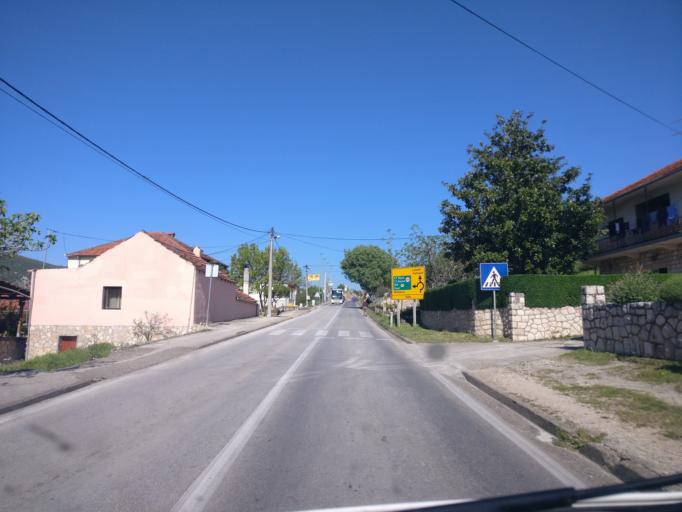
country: BA
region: Federation of Bosnia and Herzegovina
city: Capljina
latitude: 43.1410
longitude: 17.6654
